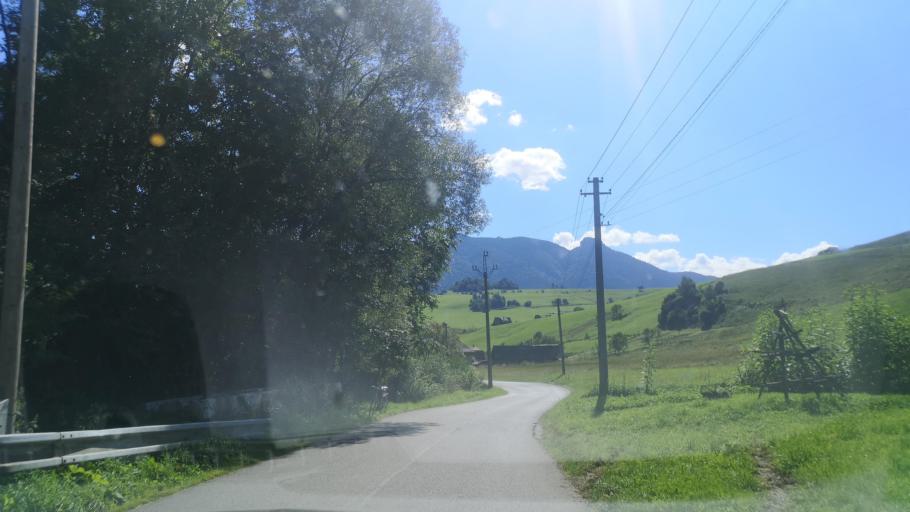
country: SK
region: Zilinsky
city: Oravska Lesna
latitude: 49.2810
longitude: 19.1339
